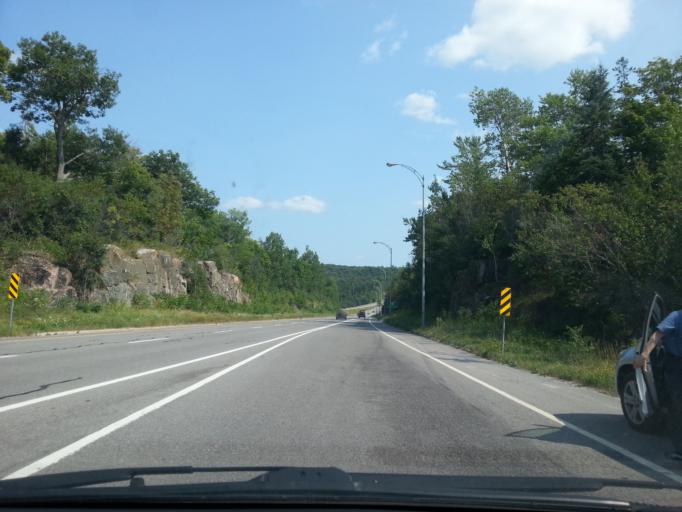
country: CA
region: Quebec
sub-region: Outaouais
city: Wakefield
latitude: 45.5709
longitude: -75.8711
